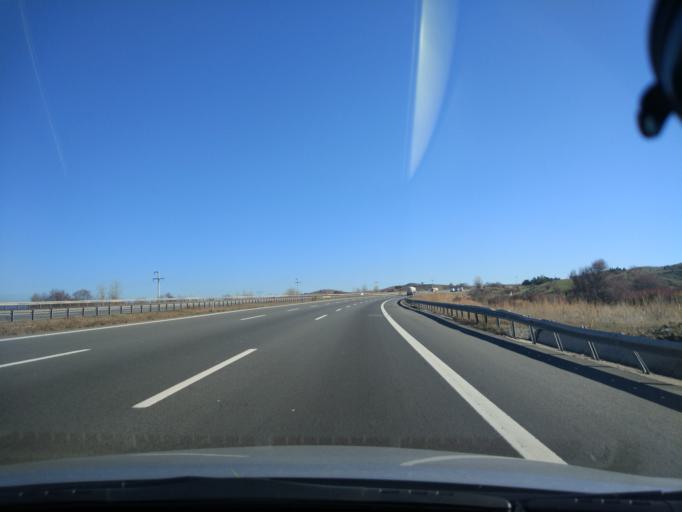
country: TR
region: Bolu
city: Yenicaga
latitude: 40.7648
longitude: 32.0509
